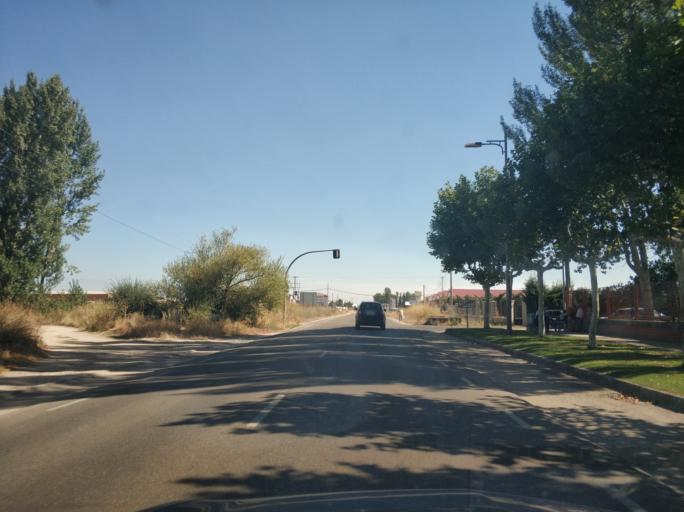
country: ES
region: Castille and Leon
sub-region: Provincia de Burgos
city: Aranda de Duero
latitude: 41.6736
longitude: -3.6730
